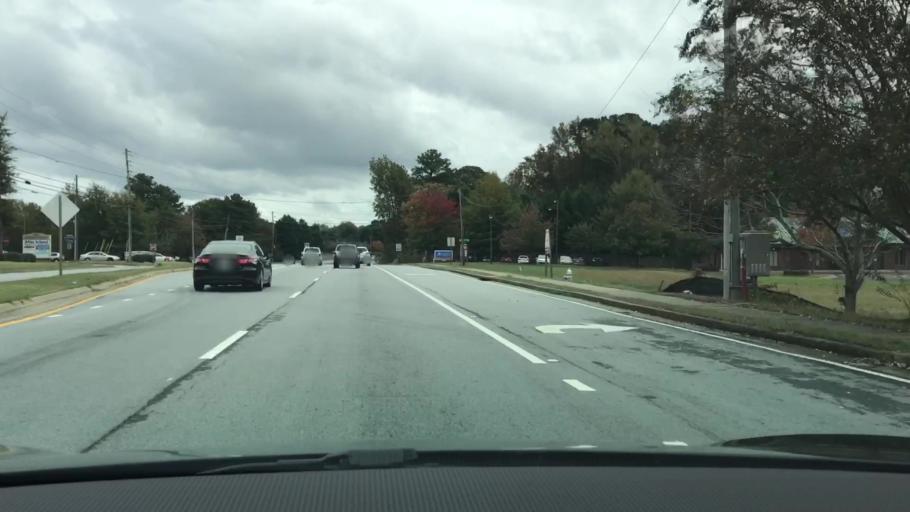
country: US
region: Georgia
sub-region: Gwinnett County
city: Suwanee
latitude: 33.9997
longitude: -84.0380
